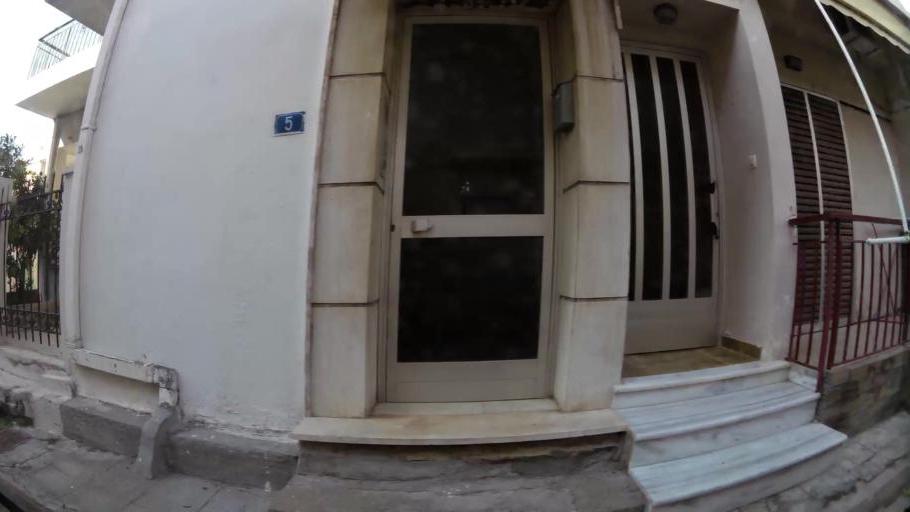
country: GR
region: Attica
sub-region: Nomarchia Dytikis Attikis
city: Zefyri
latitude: 38.0723
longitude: 23.7119
